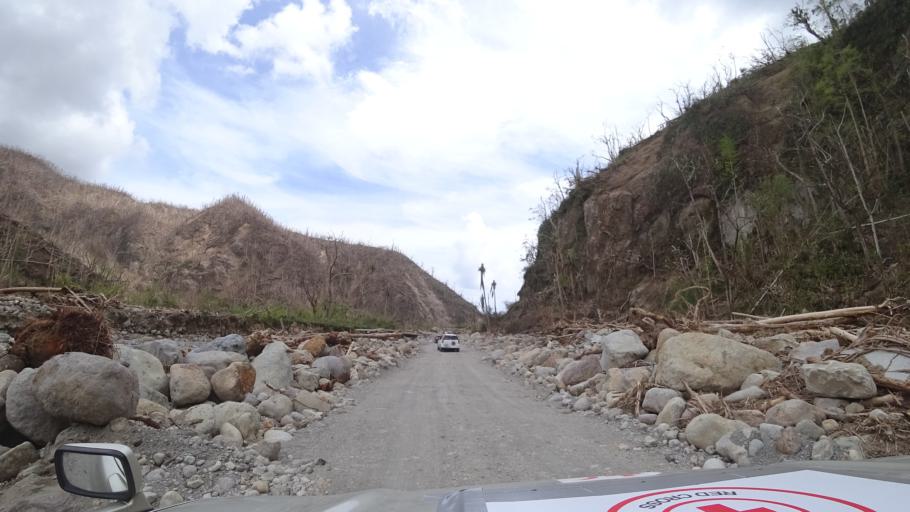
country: DM
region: Saint Patrick
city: Berekua
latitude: 15.2556
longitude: -61.3186
